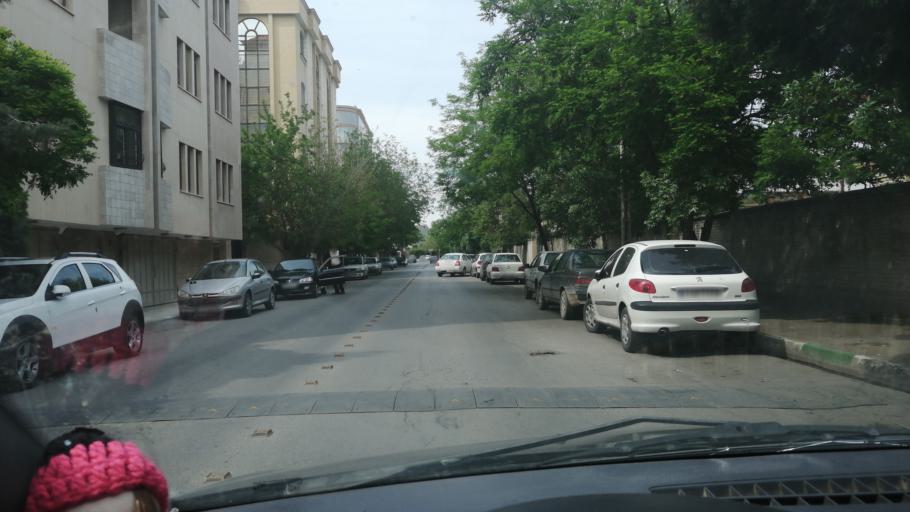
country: IR
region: Razavi Khorasan
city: Mashhad
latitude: 36.3258
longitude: 59.5670
